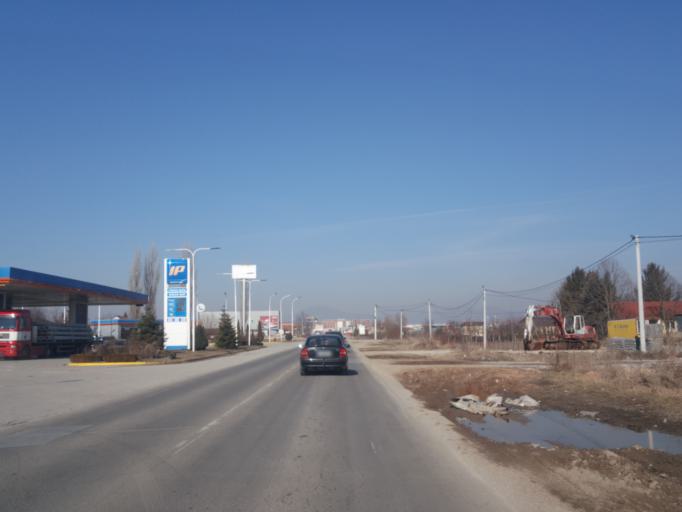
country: XK
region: Mitrovica
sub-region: Vushtrri
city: Vushtrri
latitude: 42.8085
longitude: 20.9885
